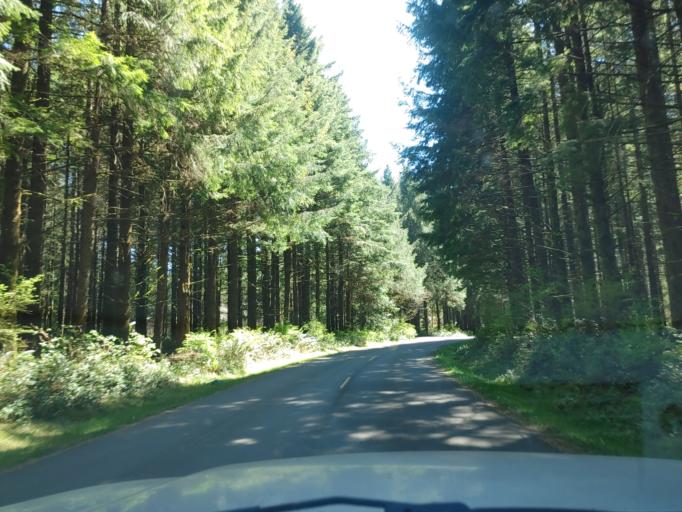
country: US
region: Oregon
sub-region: Clatsop County
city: Warrenton
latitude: 46.1361
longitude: -123.8815
